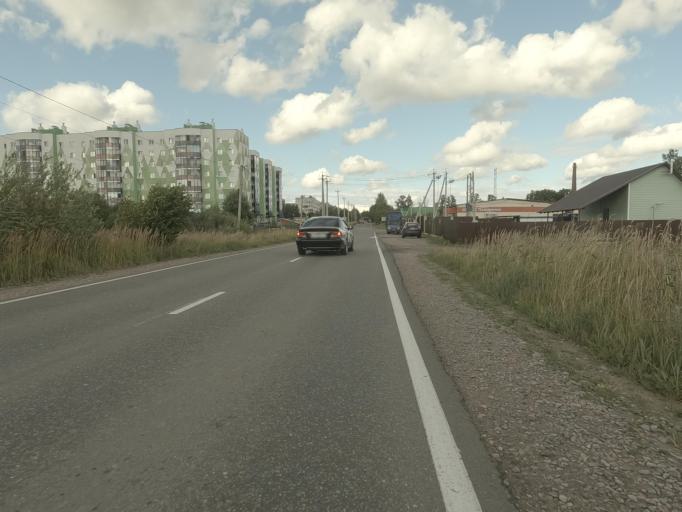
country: RU
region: Leningrad
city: Shcheglovo
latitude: 60.0234
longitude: 30.7494
